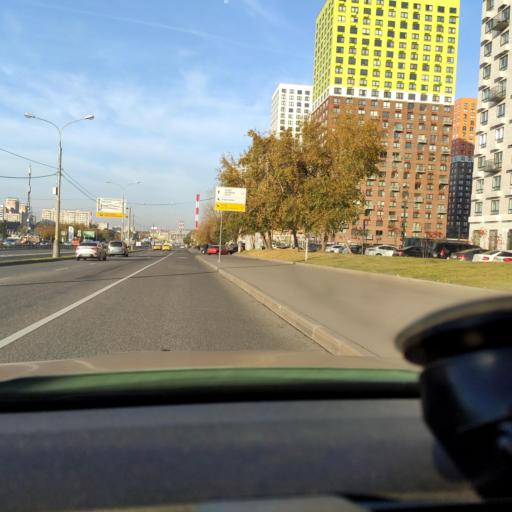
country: RU
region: Moscow
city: Mikhalkovo
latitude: 55.6615
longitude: 37.4216
